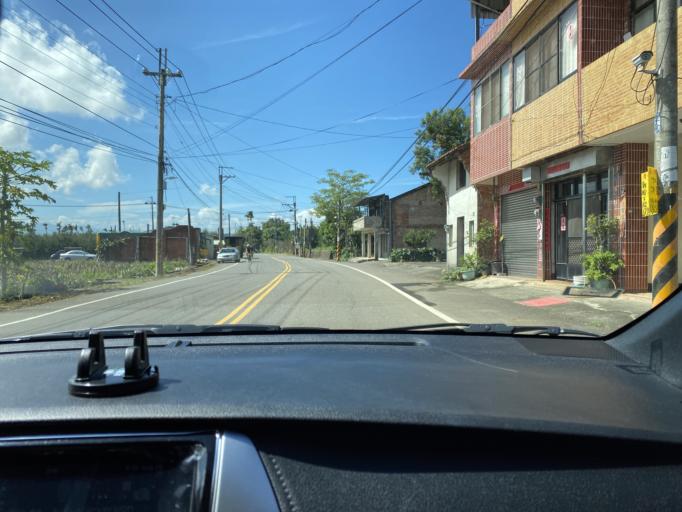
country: TW
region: Taiwan
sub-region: Nantou
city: Nantou
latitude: 23.8777
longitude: 120.6328
